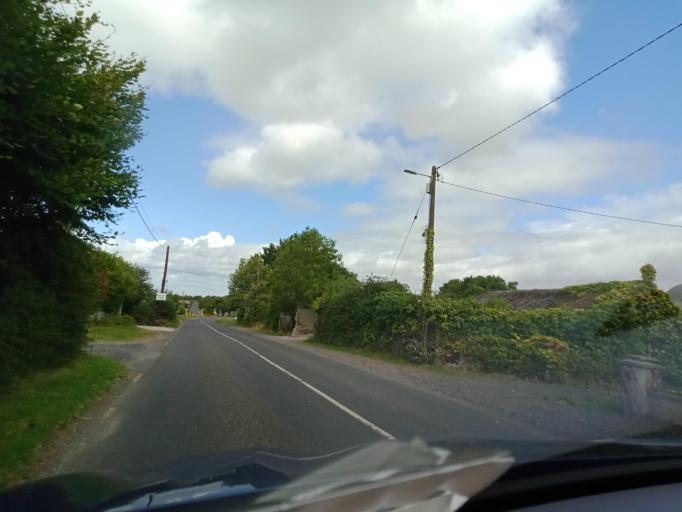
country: IE
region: Leinster
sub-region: Laois
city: Portlaoise
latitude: 52.9706
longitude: -7.2938
